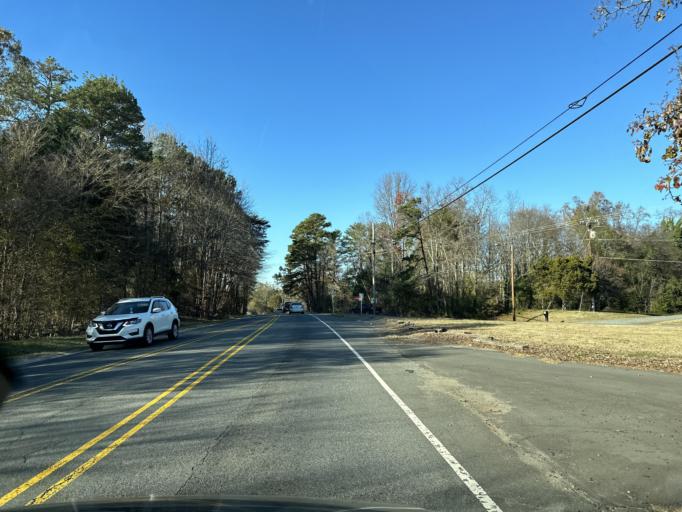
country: US
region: North Carolina
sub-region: Gaston County
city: Mount Holly
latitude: 35.3092
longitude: -80.9391
